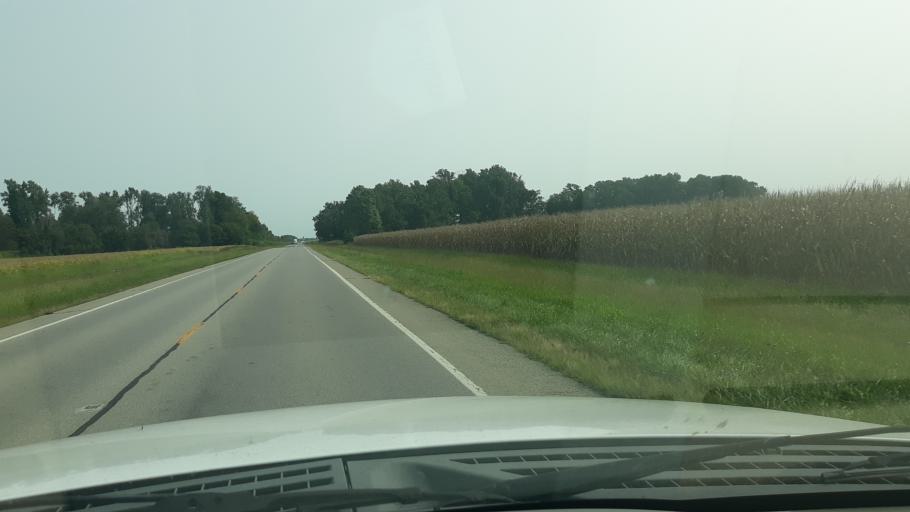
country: US
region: Illinois
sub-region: White County
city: Carmi
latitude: 38.1197
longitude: -88.1115
